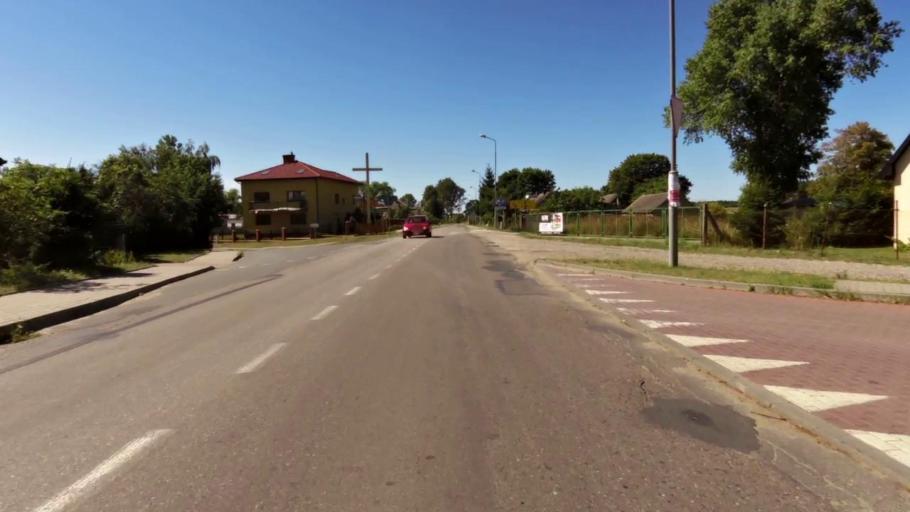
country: PL
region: West Pomeranian Voivodeship
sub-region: Powiat szczecinecki
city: Szczecinek
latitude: 53.7172
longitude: 16.6335
